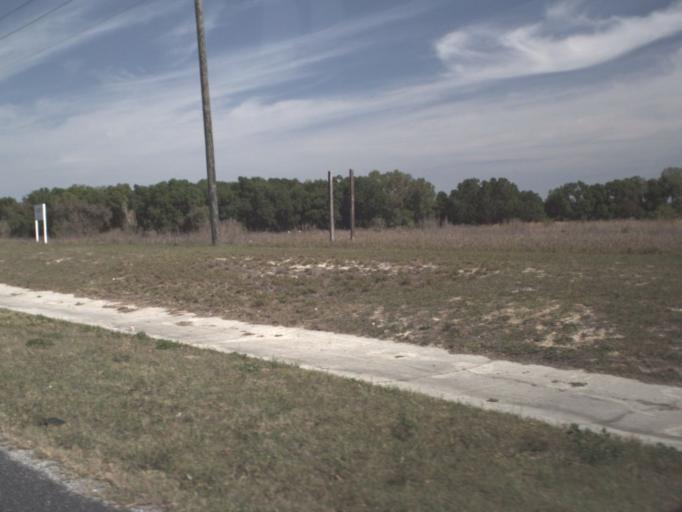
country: US
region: Florida
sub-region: Sumter County
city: The Villages
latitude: 28.9716
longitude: -81.9769
